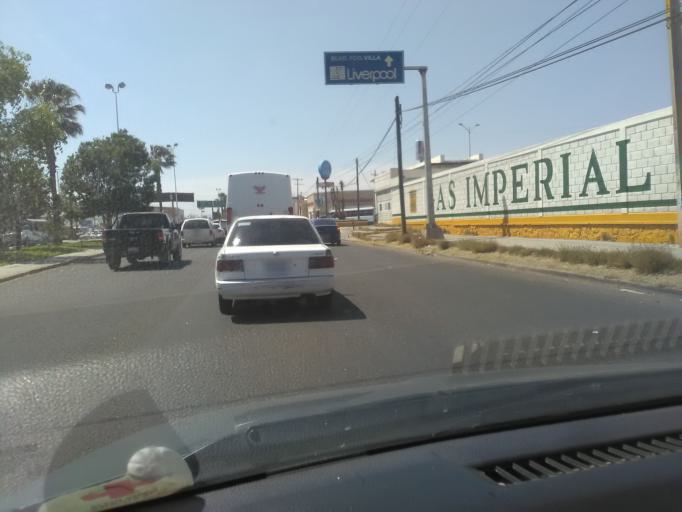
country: MX
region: Durango
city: Victoria de Durango
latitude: 24.0312
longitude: -104.6190
